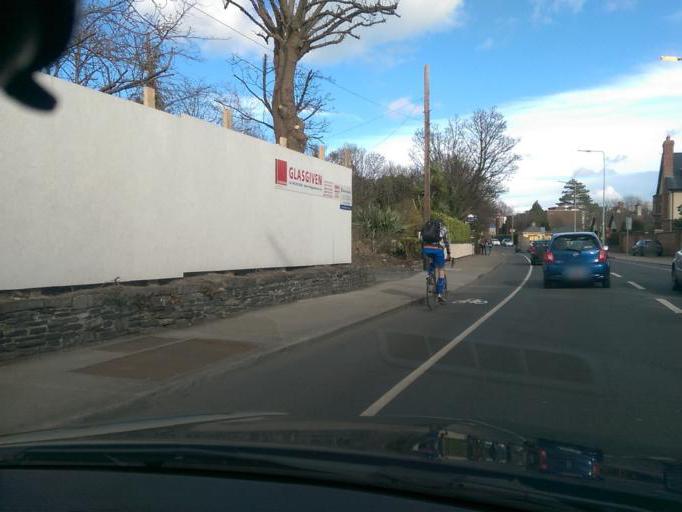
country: IE
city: Donnycarney
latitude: 53.3672
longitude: -6.2166
